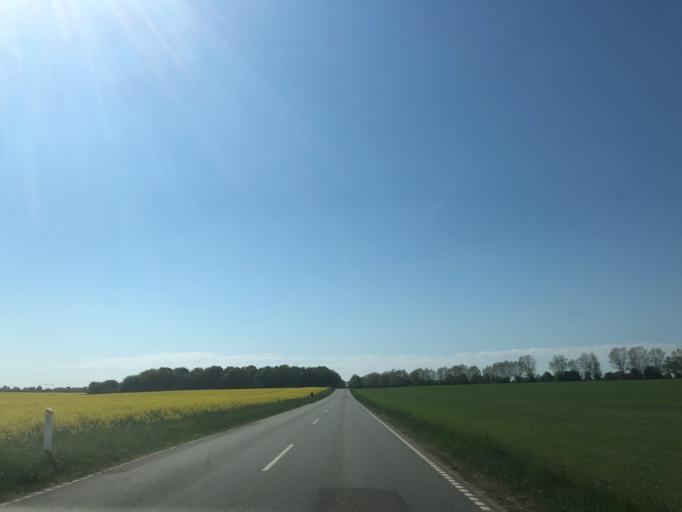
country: DK
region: Zealand
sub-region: Greve Kommune
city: Tune
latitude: 55.6254
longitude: 12.2051
